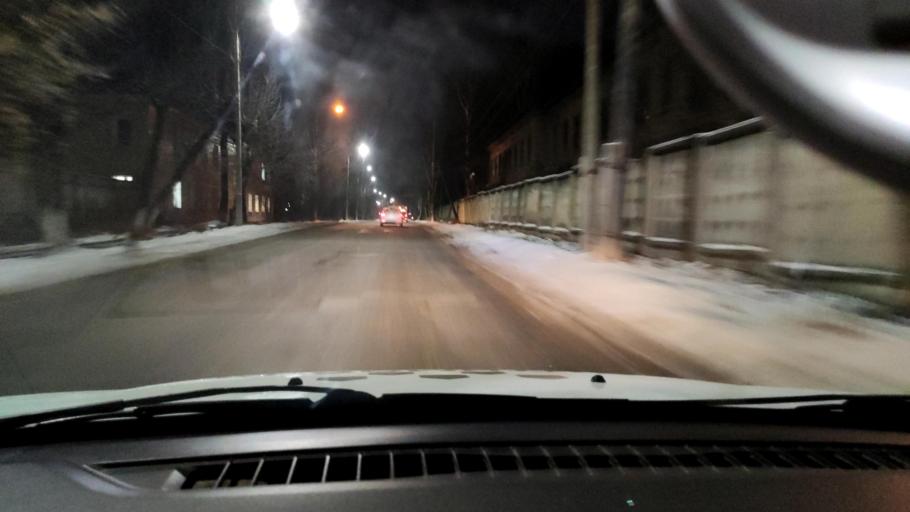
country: RU
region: Perm
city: Kultayevo
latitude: 57.9888
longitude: 55.9253
